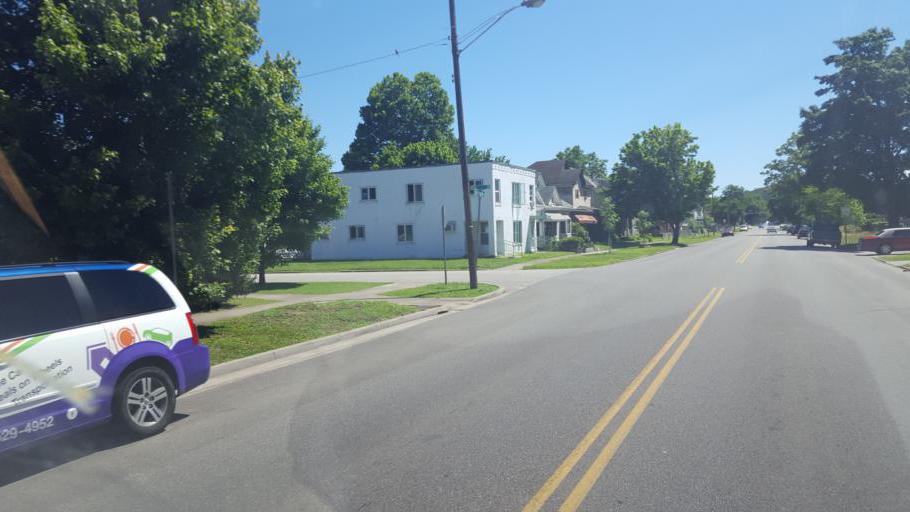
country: US
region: West Virginia
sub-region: Cabell County
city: Huntington
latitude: 38.4167
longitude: -82.4247
